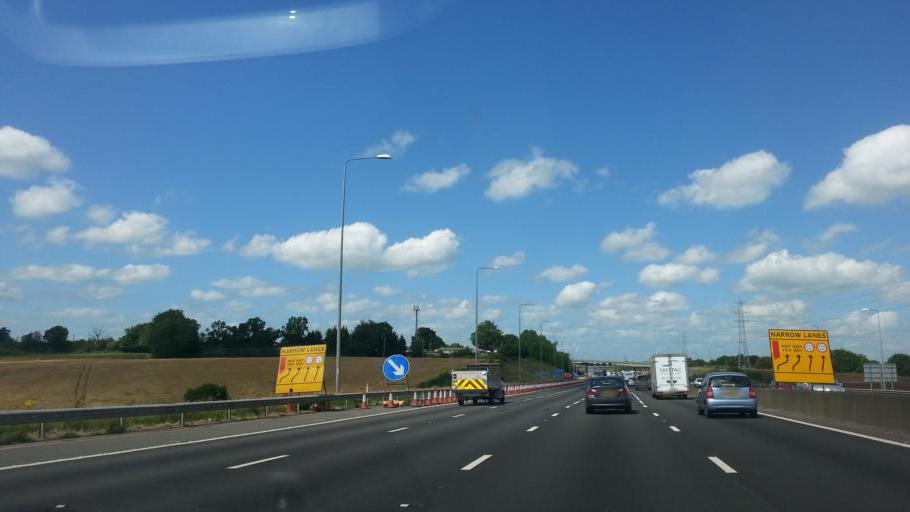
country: GB
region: England
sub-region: Buckinghamshire
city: Chalfont Saint Peter
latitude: 51.6094
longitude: -0.5279
